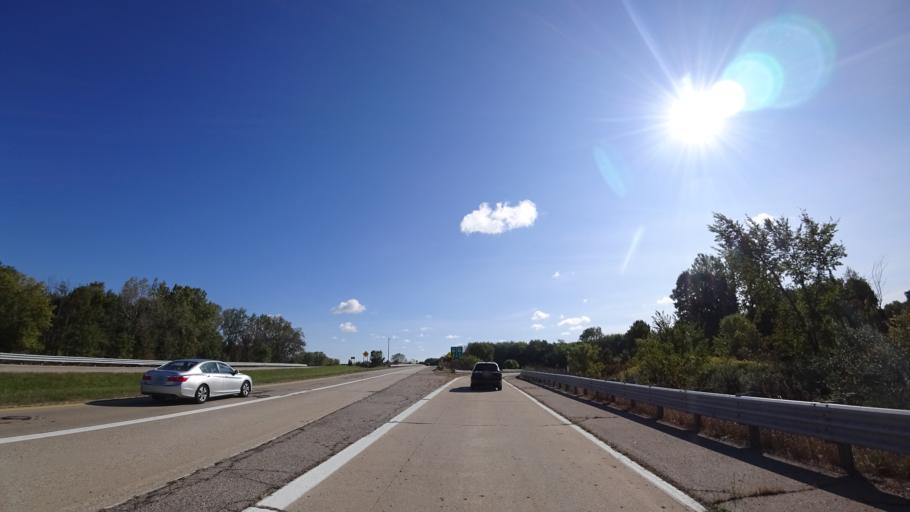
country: US
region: Michigan
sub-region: Berrien County
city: Benton Heights
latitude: 42.1190
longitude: -86.3942
